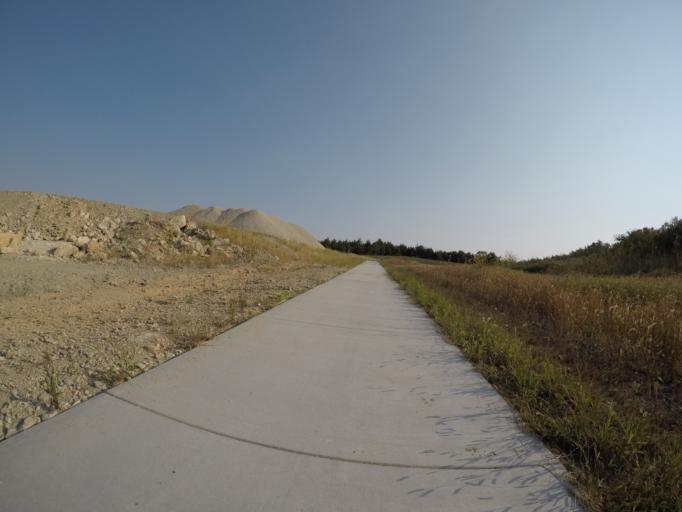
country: US
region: Kansas
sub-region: Riley County
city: Manhattan
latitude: 39.1758
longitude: -96.6424
